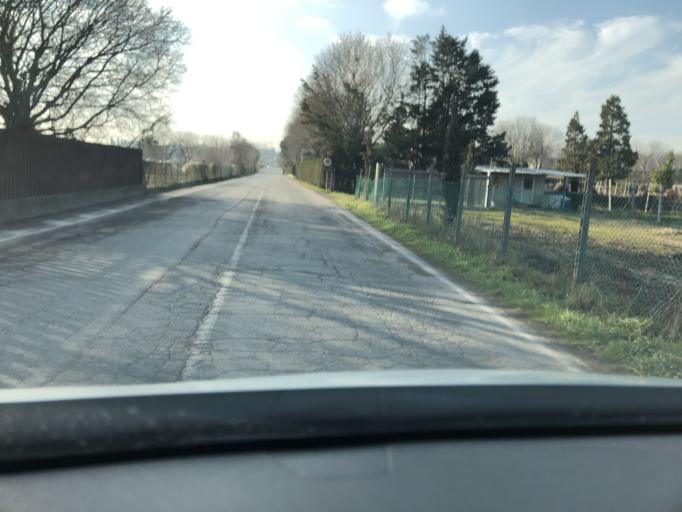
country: IT
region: Veneto
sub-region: Provincia di Verona
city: Sommacampagna
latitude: 45.4129
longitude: 10.8605
